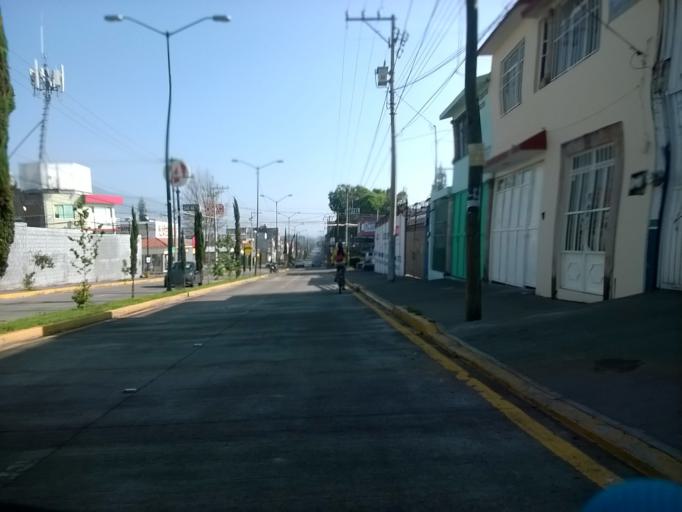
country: MX
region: Michoacan
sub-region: Morelia
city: Morelos
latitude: 19.6780
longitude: -101.2256
